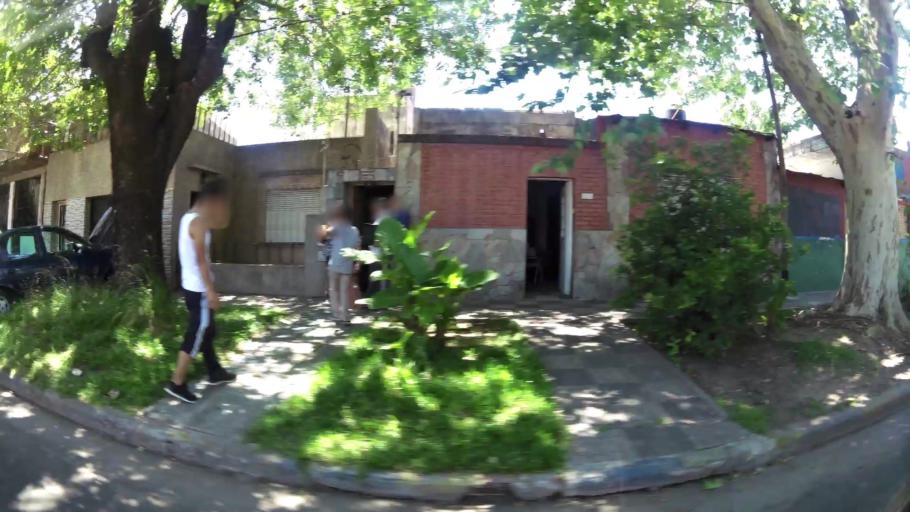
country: AR
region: Santa Fe
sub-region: Departamento de Rosario
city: Rosario
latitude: -32.9443
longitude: -60.7136
